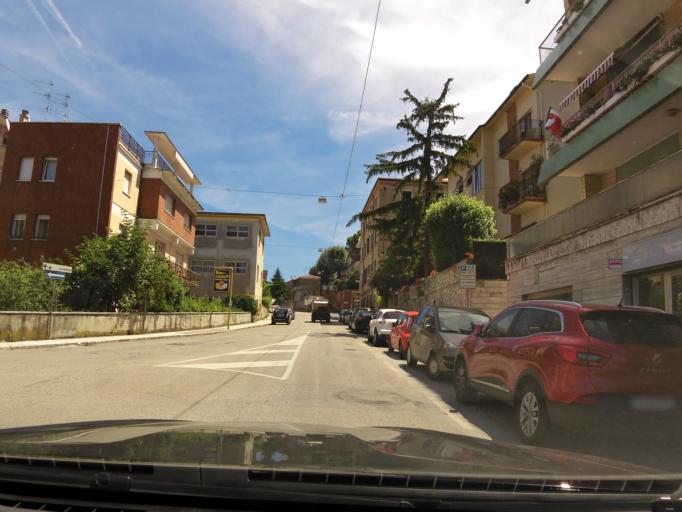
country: IT
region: The Marches
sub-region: Provincia di Ancona
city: Le Grazie di Ancona
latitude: 43.6140
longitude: 13.5251
